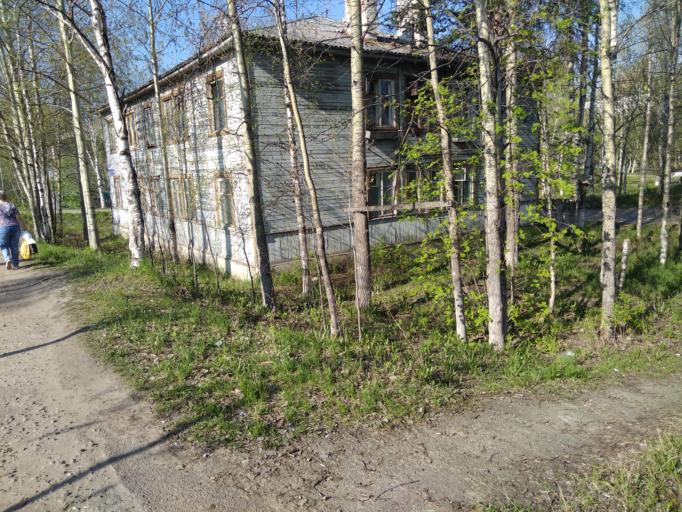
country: RU
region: Komi Republic
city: Pechora
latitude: 65.1209
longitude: 57.1543
